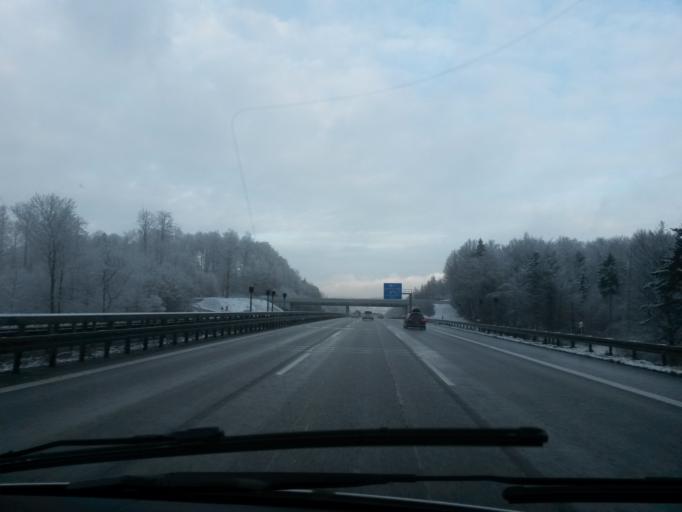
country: DE
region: Baden-Wuerttemberg
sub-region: Regierungsbezirk Stuttgart
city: Leonberg
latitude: 48.7512
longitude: 9.0342
